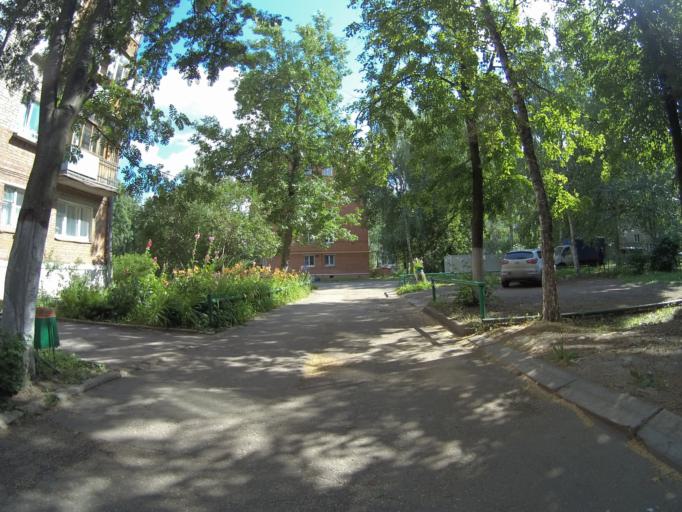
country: RU
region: Vladimir
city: Vladimir
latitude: 56.1402
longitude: 40.4228
